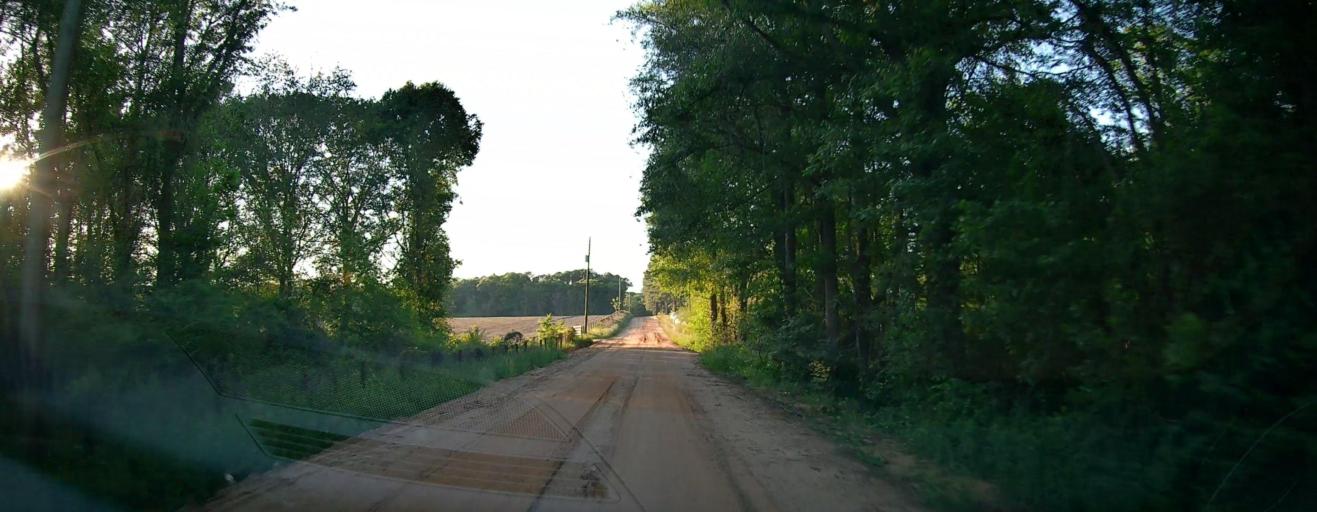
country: US
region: Georgia
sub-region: Irwin County
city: Ocilla
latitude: 31.6450
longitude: -83.2226
